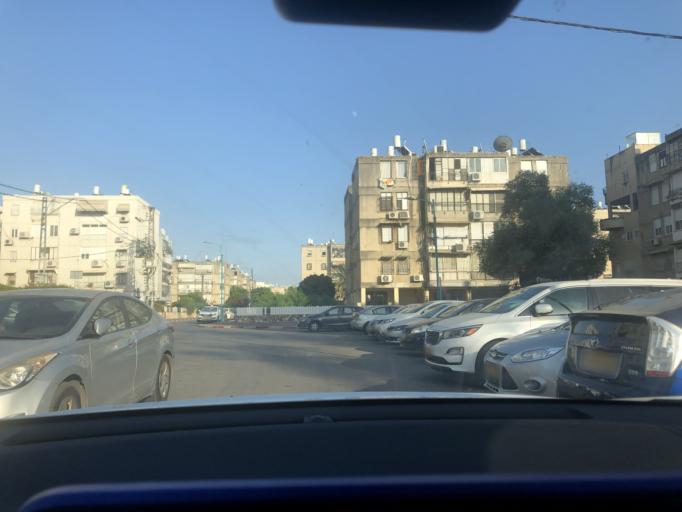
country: IL
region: Central District
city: Lod
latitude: 31.9528
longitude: 34.8880
